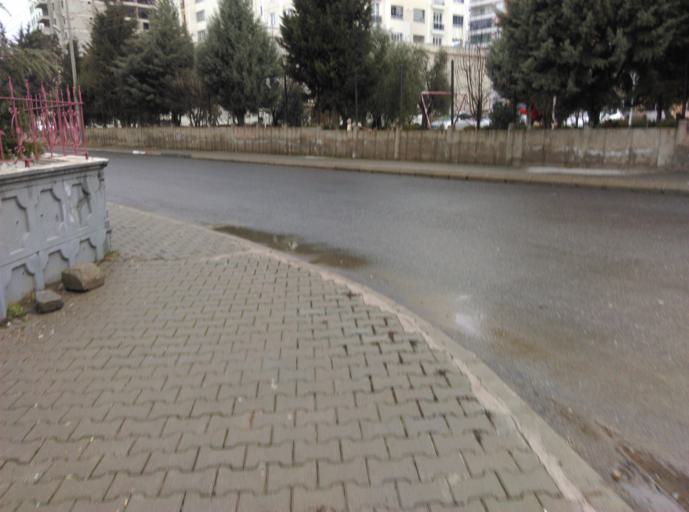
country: TR
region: Kahramanmaras
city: Kahramanmaras
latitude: 37.5836
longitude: 36.8963
